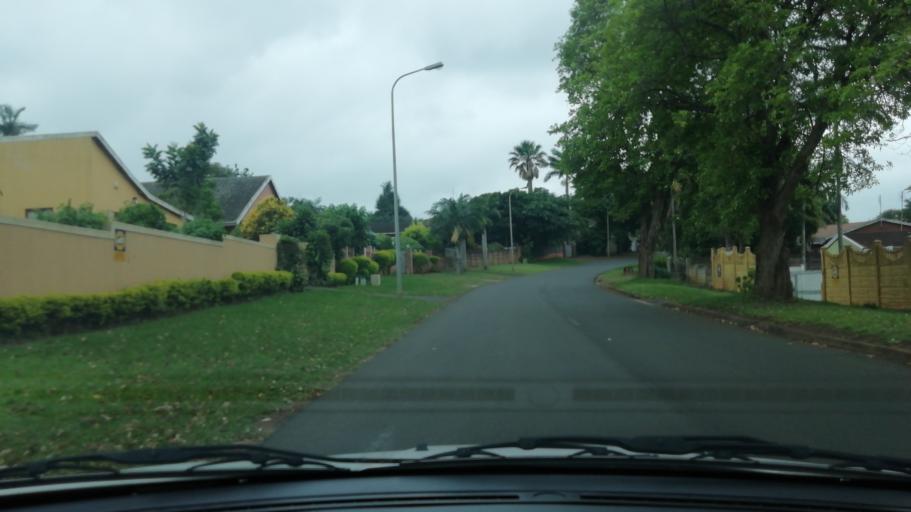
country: ZA
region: KwaZulu-Natal
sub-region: uThungulu District Municipality
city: Empangeni
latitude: -28.7660
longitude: 31.8923
